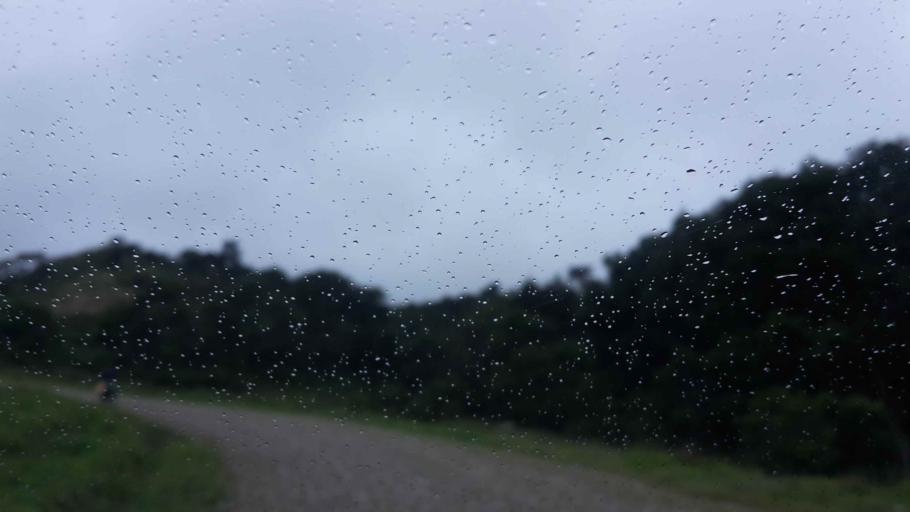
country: BO
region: Cochabamba
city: Colomi
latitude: -17.1306
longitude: -65.9355
